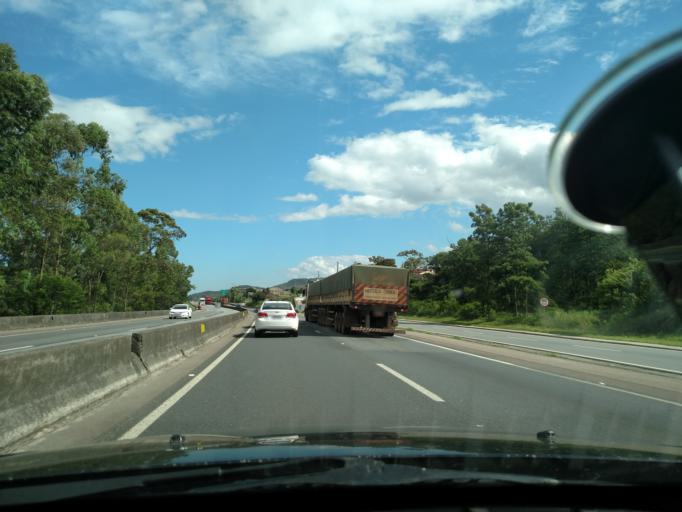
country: BR
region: Santa Catarina
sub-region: Biguacu
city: Biguacu
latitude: -27.3888
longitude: -48.6320
